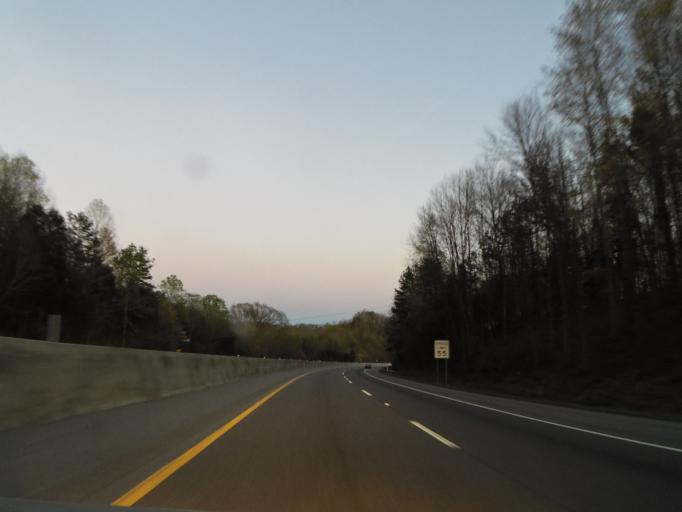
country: US
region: Tennessee
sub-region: Anderson County
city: Norris
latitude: 36.1161
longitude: -84.0290
